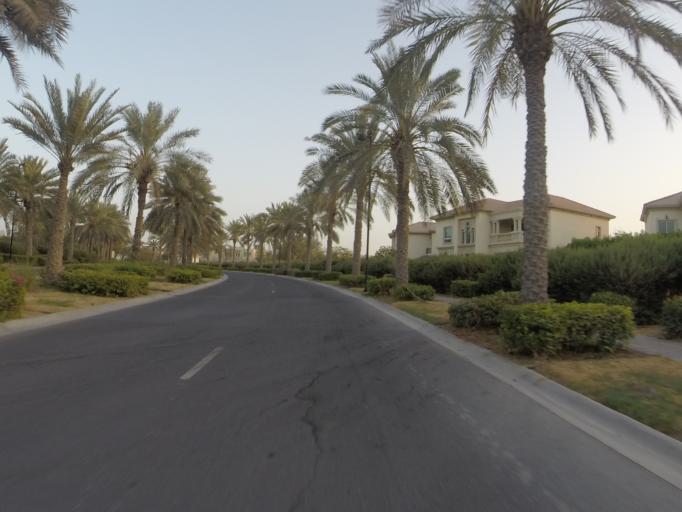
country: AE
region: Dubai
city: Dubai
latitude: 25.0532
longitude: 55.1654
